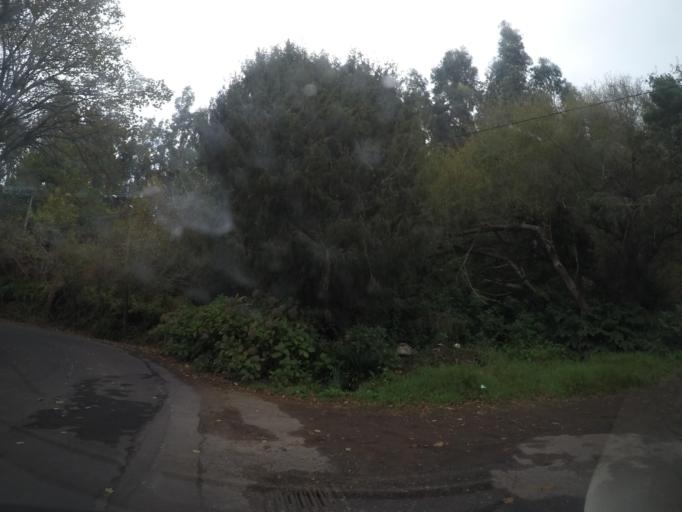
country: PT
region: Madeira
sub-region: Porto Moniz
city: Porto Moniz
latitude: 32.8391
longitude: -17.2088
